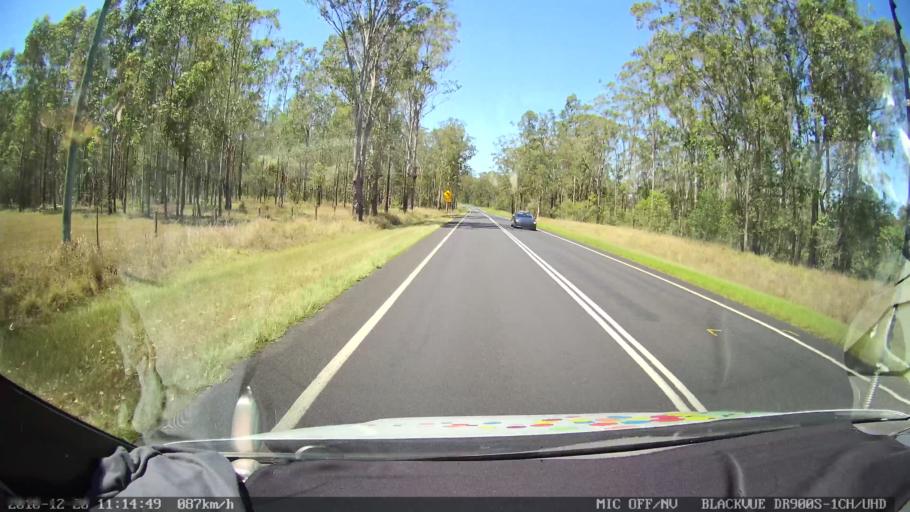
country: AU
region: New South Wales
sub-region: Richmond Valley
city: Casino
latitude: -29.0051
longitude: 153.0071
